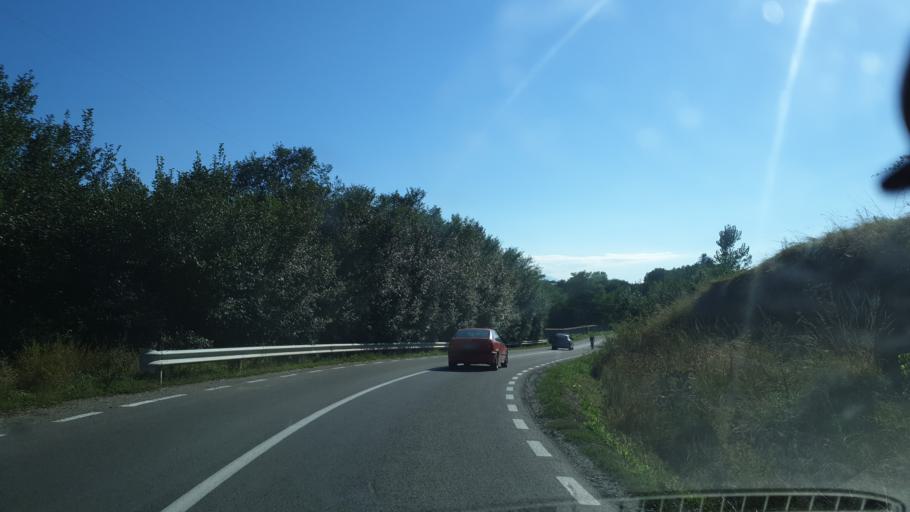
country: RO
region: Covasna
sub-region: Comuna Ilieni
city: Ilieni
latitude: 45.7869
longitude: 25.7608
